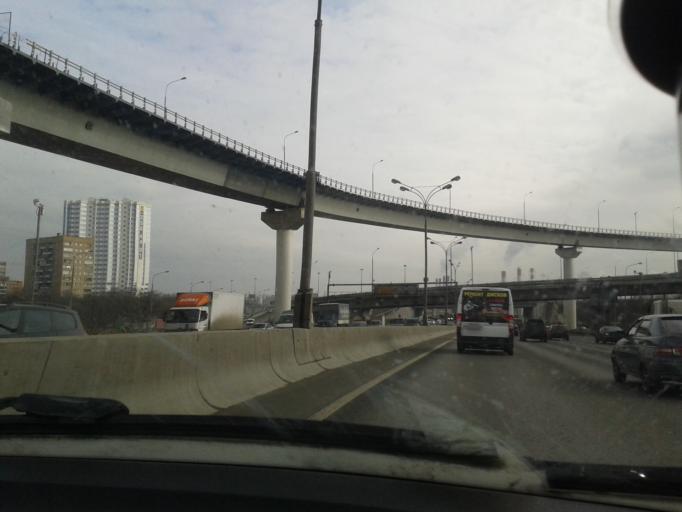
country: RU
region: Moskovskaya
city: Levoberezhnaya
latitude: 55.8856
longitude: 37.4766
